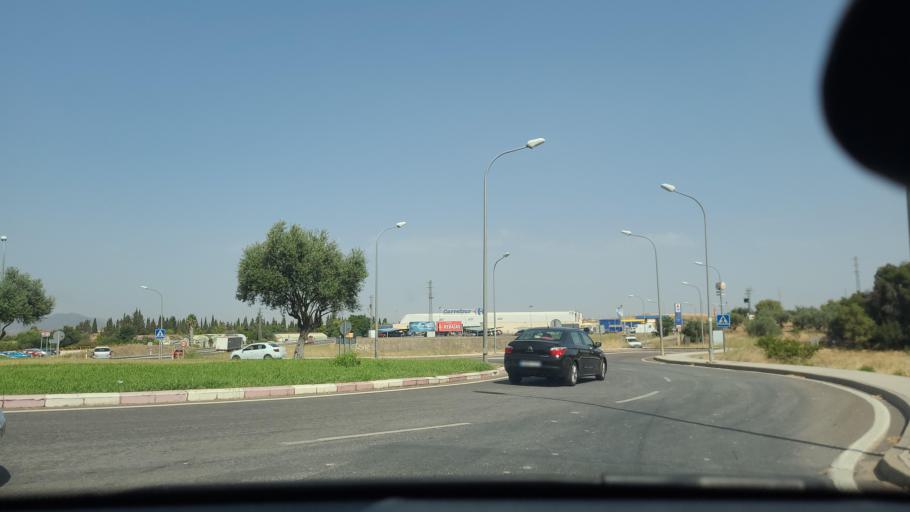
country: ES
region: Extremadura
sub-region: Provincia de Badajoz
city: Zafra
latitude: 38.4314
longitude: -6.4202
